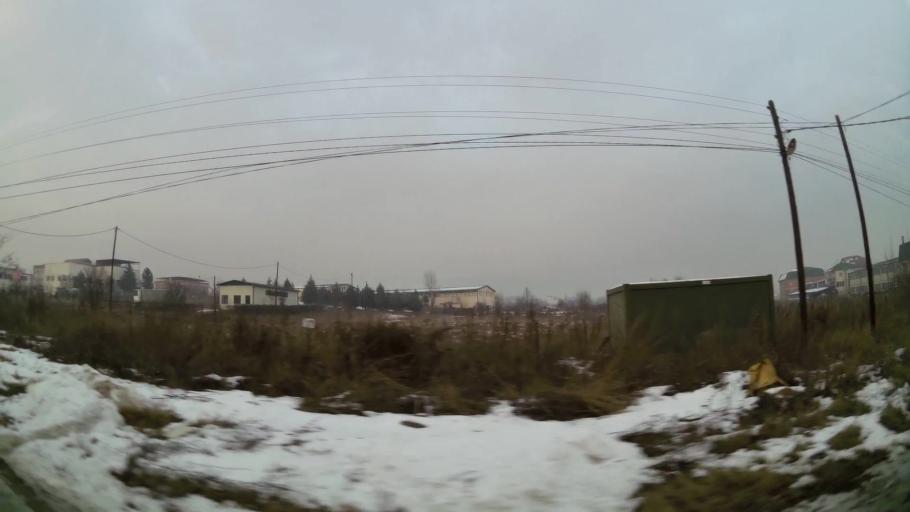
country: MK
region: Suto Orizari
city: Suto Orizare
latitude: 42.0382
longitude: 21.3980
